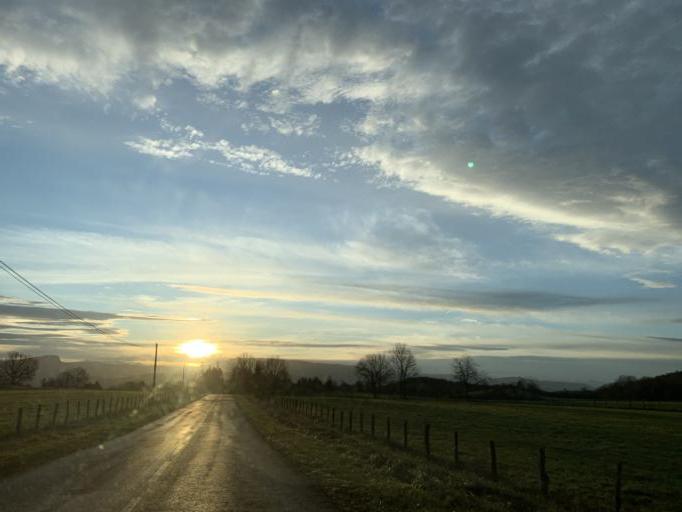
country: FR
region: Rhone-Alpes
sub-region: Departement de l'Ain
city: Virieu-le-Grand
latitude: 45.7959
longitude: 5.6361
